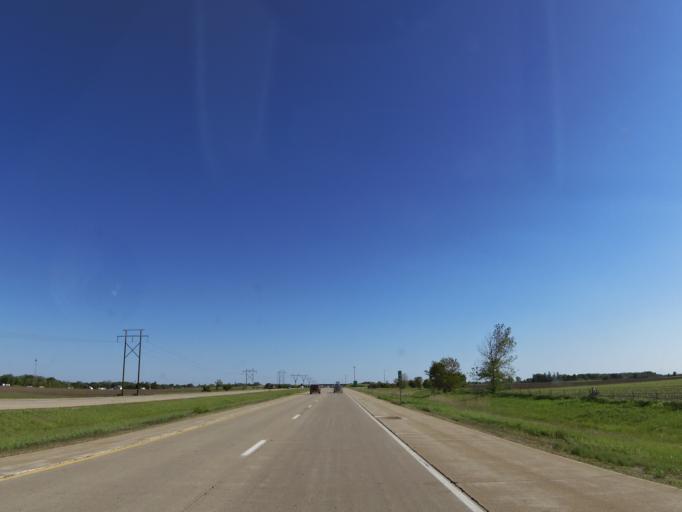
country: US
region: Illinois
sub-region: LaSalle County
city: Oglesby
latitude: 41.2300
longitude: -89.0781
